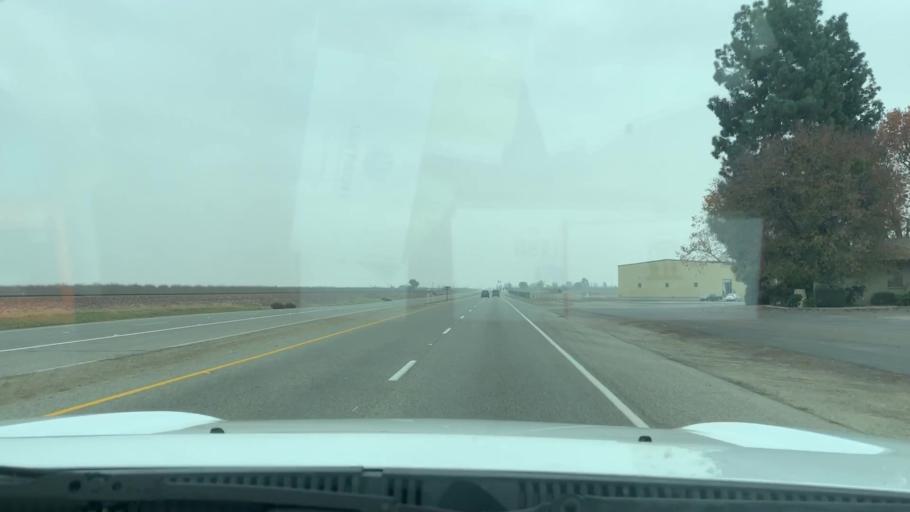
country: US
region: California
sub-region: Kern County
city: Shafter
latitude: 35.5272
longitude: -119.3039
